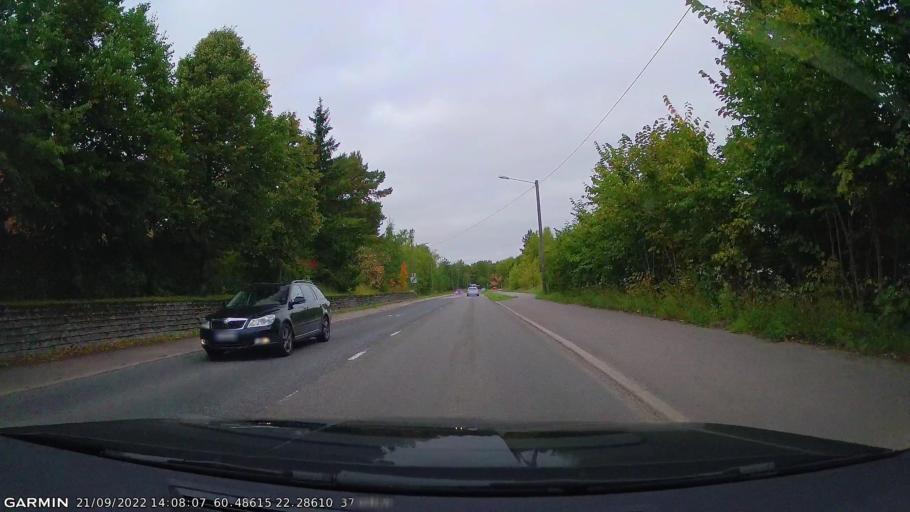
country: FI
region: Varsinais-Suomi
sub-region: Turku
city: Turku
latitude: 60.4862
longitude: 22.2859
